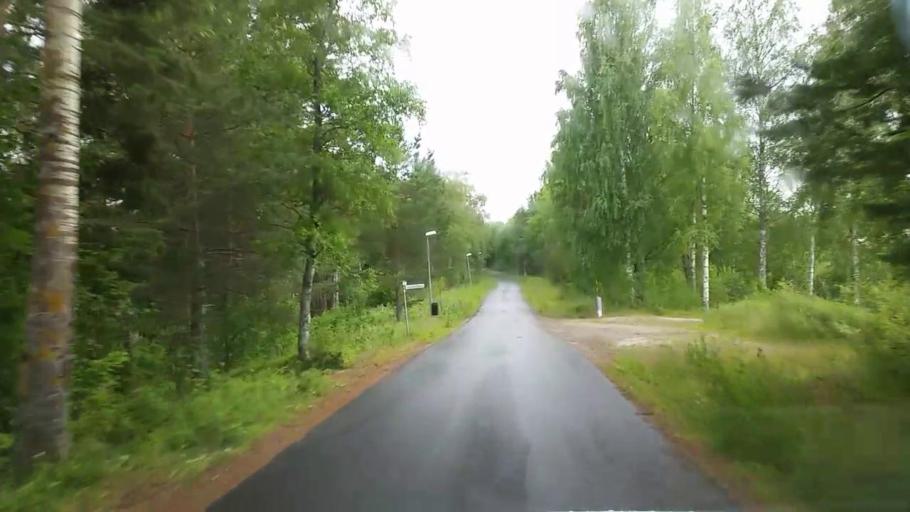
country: SE
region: Gaevleborg
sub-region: Ljusdals Kommun
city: Jaervsoe
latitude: 61.7165
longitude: 16.1782
